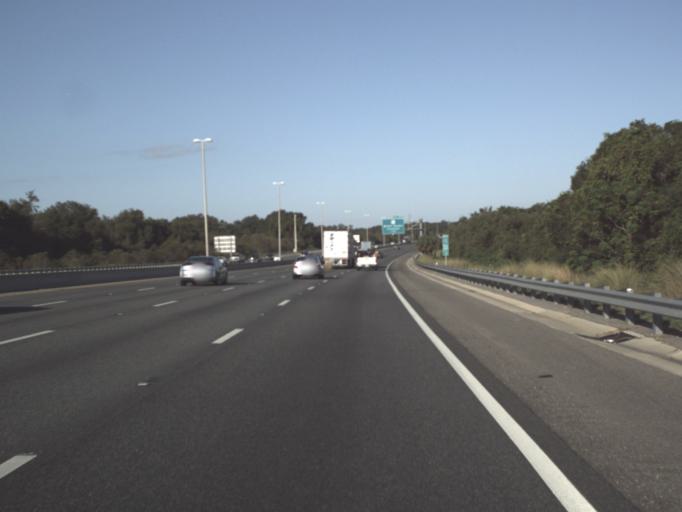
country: US
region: Florida
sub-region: Orange County
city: Oakland
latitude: 28.5453
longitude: -81.6110
